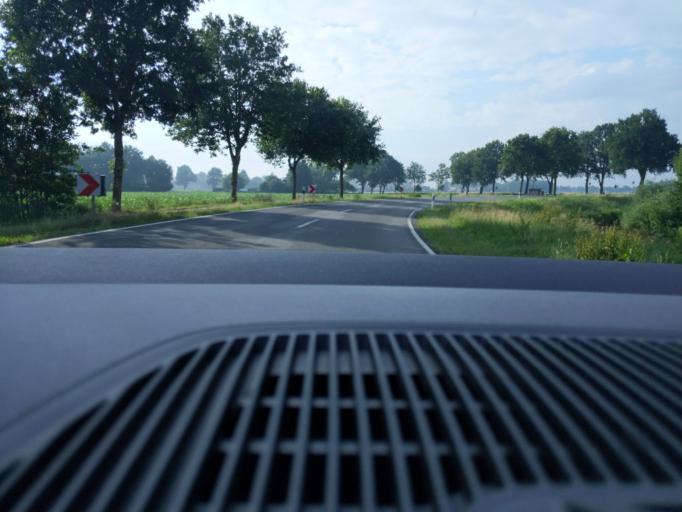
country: NL
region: Drenthe
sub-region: Gemeente Emmen
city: Emmer-Compascuum
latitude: 52.8027
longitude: 7.1066
